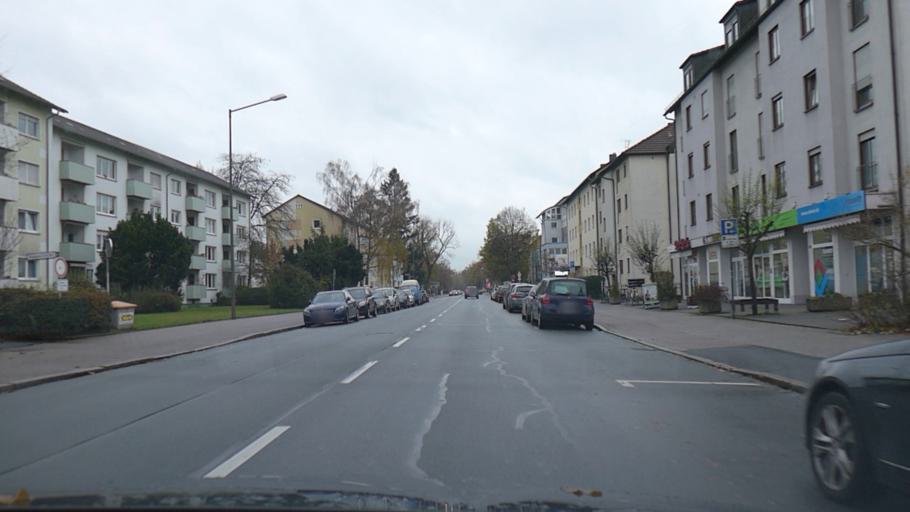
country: DE
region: Bavaria
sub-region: Regierungsbezirk Mittelfranken
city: Erlangen
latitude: 49.5907
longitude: 11.0172
